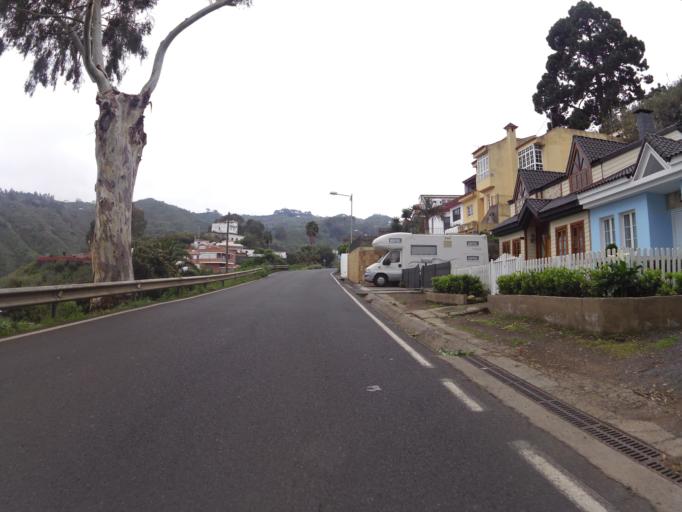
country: ES
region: Canary Islands
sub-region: Provincia de Las Palmas
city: Teror
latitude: 28.0650
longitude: -15.5386
